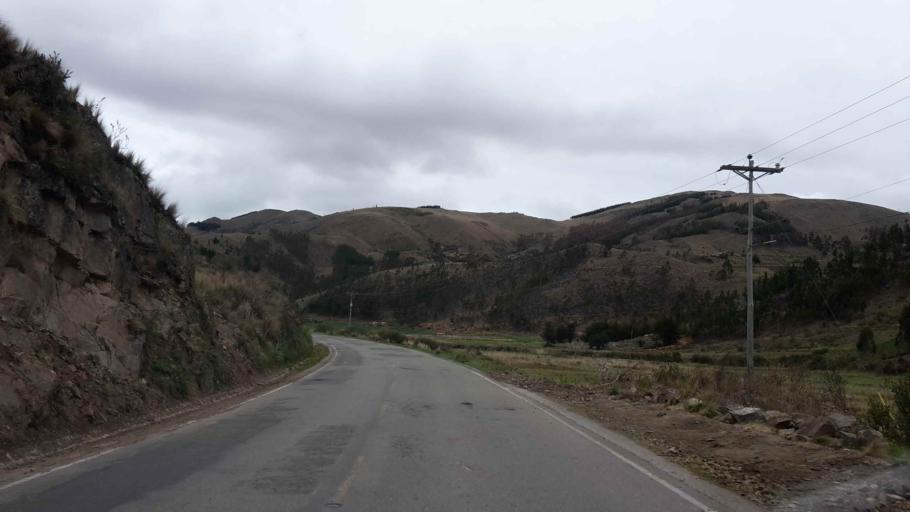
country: BO
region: Cochabamba
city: Arani
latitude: -17.4848
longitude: -65.5560
